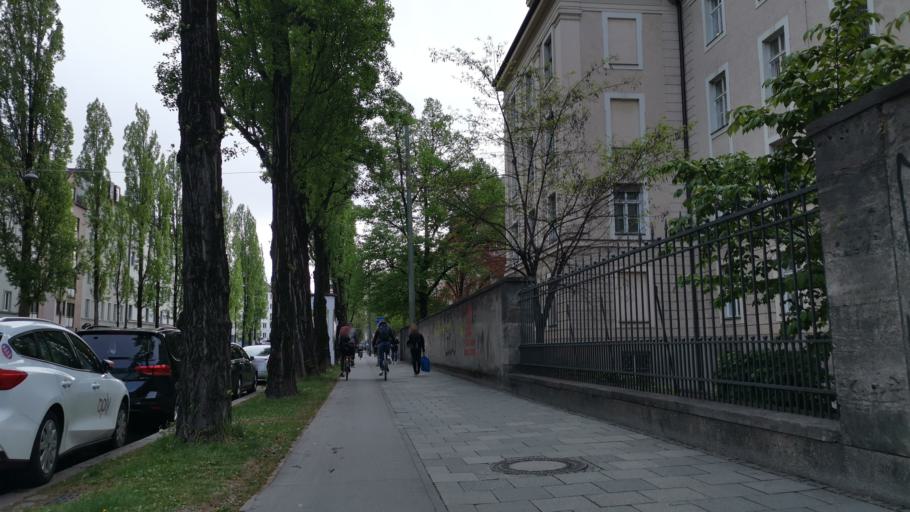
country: DE
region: Bavaria
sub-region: Upper Bavaria
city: Munich
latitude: 48.1306
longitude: 11.5604
